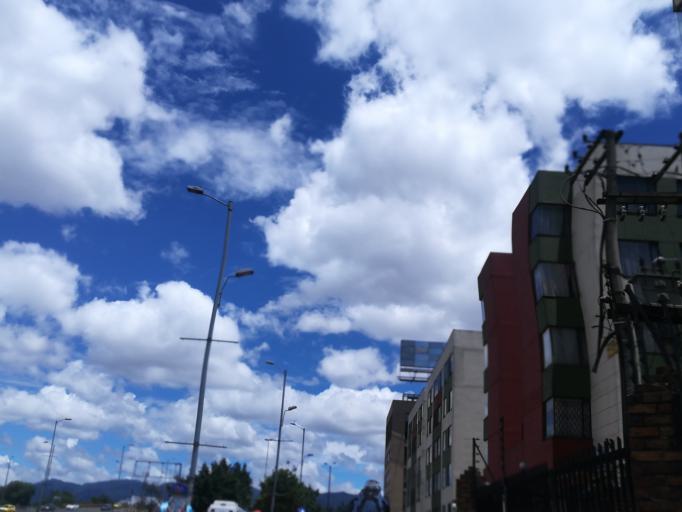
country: CO
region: Bogota D.C.
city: Bogota
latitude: 4.6303
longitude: -74.1402
